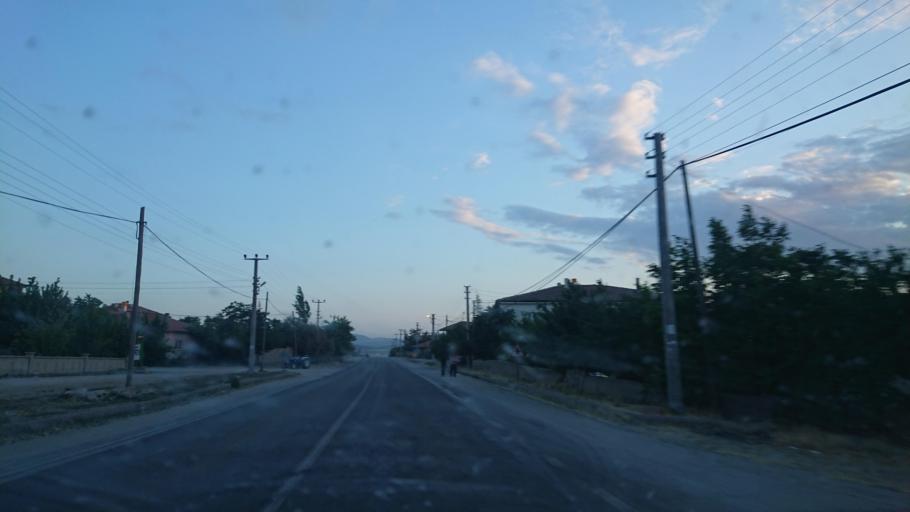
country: TR
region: Aksaray
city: Balci
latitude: 38.7906
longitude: 34.1231
